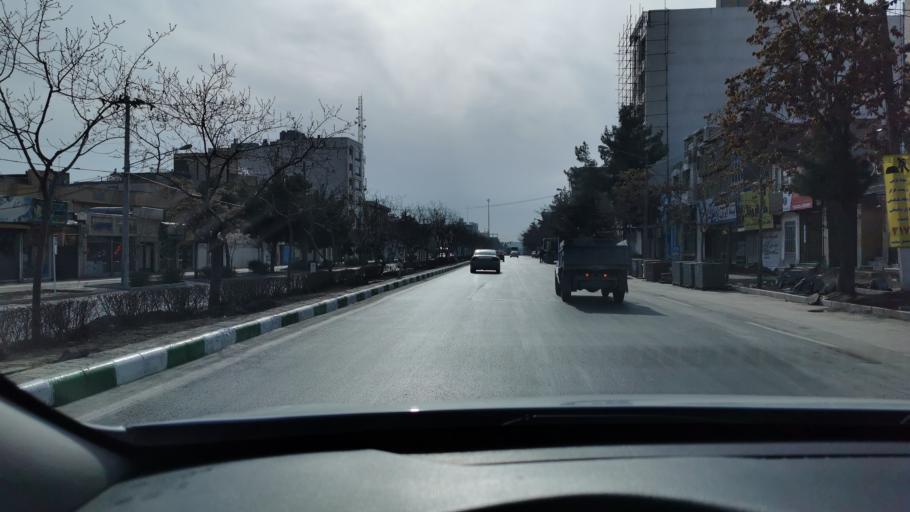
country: IR
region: Razavi Khorasan
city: Mashhad
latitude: 36.2926
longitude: 59.5349
